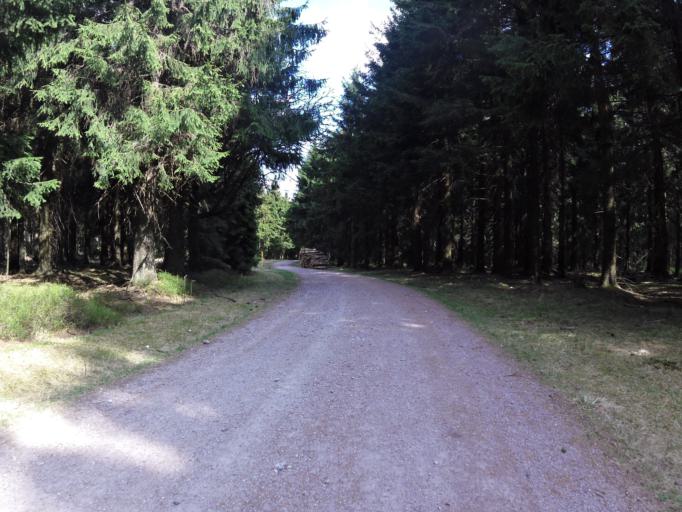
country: DE
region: Thuringia
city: Oberhof
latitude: 50.7002
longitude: 10.7080
